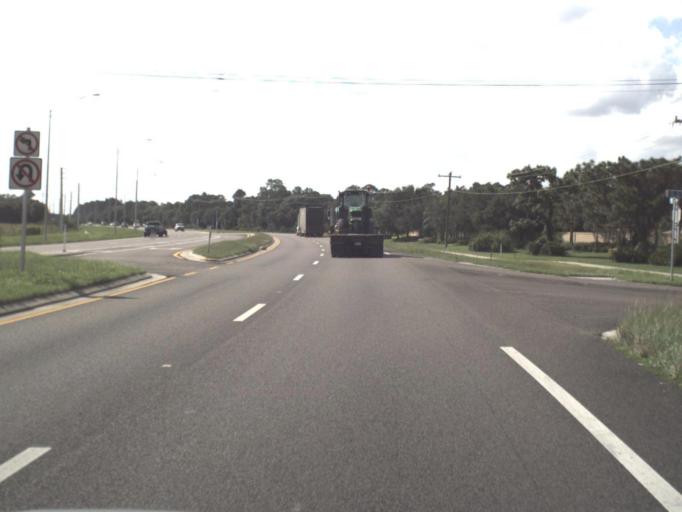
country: US
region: Florida
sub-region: Manatee County
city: Ellenton
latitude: 27.4837
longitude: -82.4085
